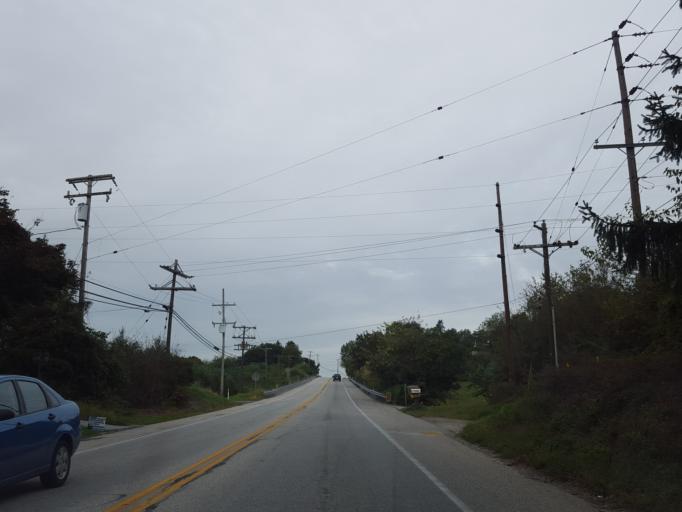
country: US
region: Pennsylvania
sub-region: York County
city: Shiloh
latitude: 39.9239
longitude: -76.8009
